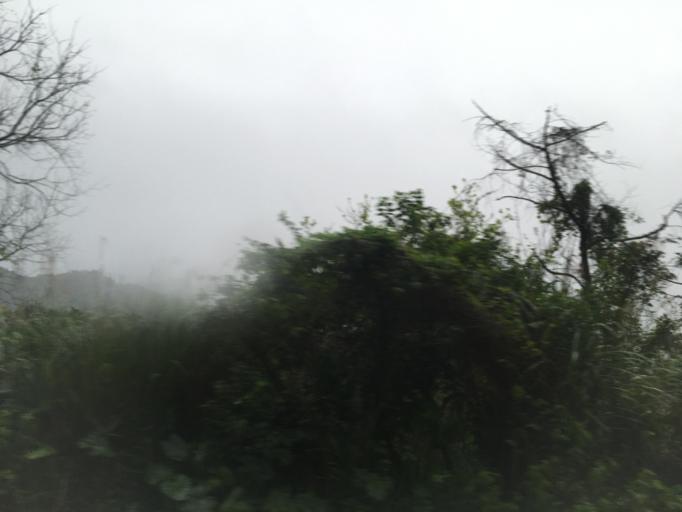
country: TW
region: Taiwan
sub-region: Keelung
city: Keelung
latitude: 25.0209
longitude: 121.8936
